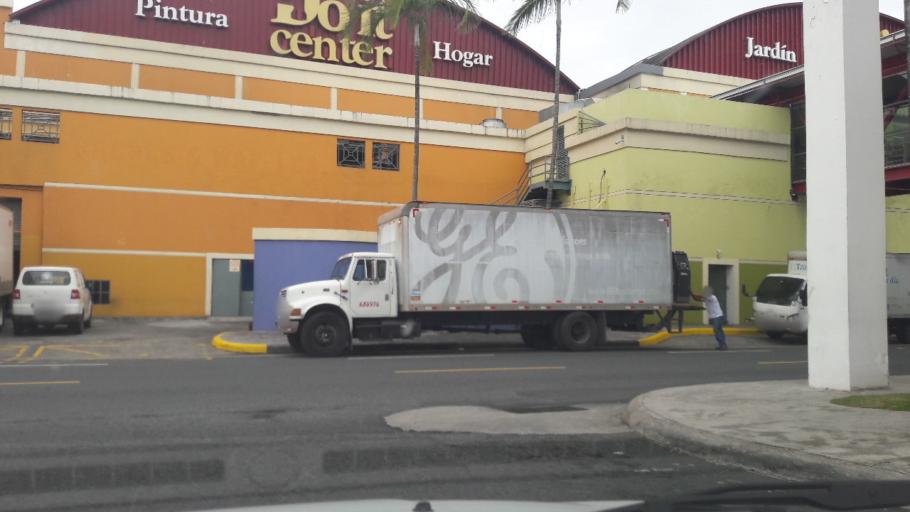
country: PA
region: Panama
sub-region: Distrito de Panama
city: Ancon
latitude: 8.9775
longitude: -79.5524
